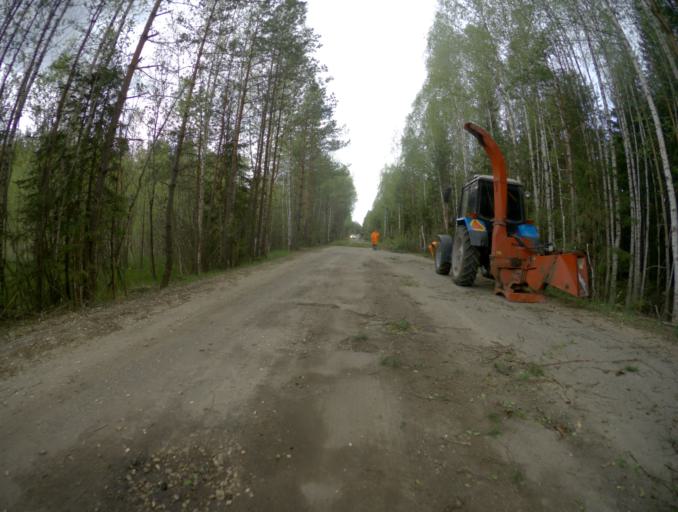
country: RU
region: Vladimir
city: Velikodvorskiy
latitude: 55.2450
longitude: 40.7103
